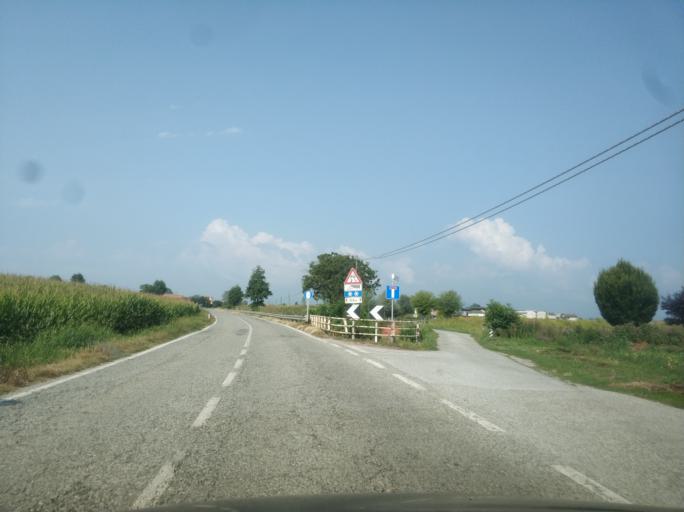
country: IT
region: Piedmont
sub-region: Provincia di Cuneo
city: Centallo
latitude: 44.5121
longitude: 7.6417
